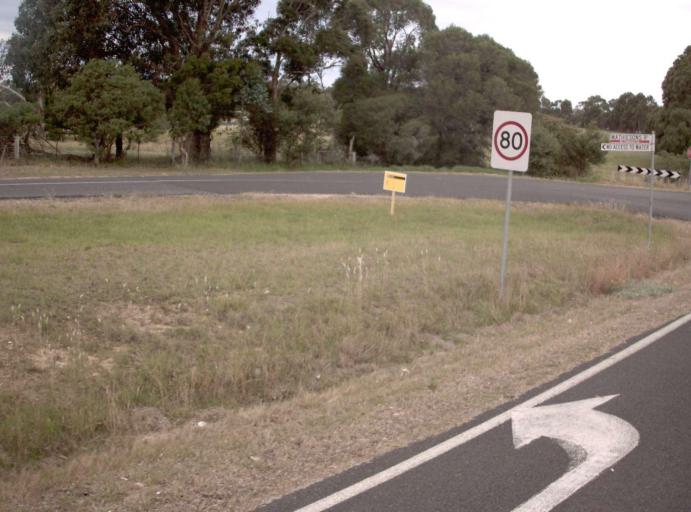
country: AU
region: Victoria
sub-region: East Gippsland
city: Bairnsdale
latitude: -37.8938
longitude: 147.6585
